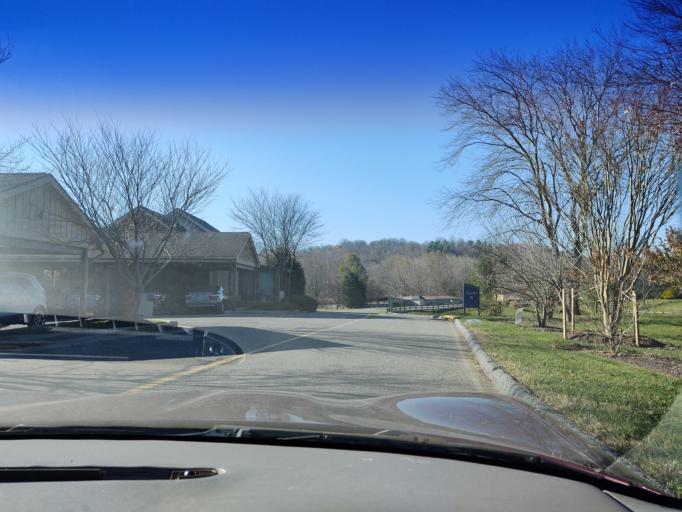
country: US
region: Maryland
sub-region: Baltimore County
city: Hunt Valley
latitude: 39.5002
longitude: -76.6452
